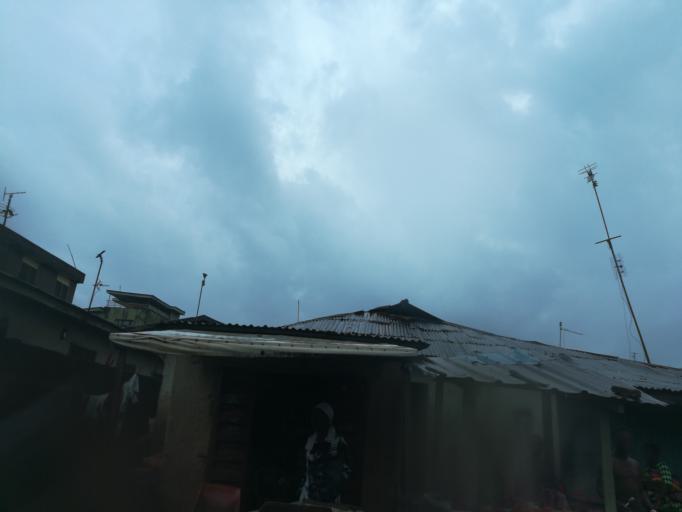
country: NG
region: Lagos
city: Oshodi
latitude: 6.5741
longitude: 3.3430
